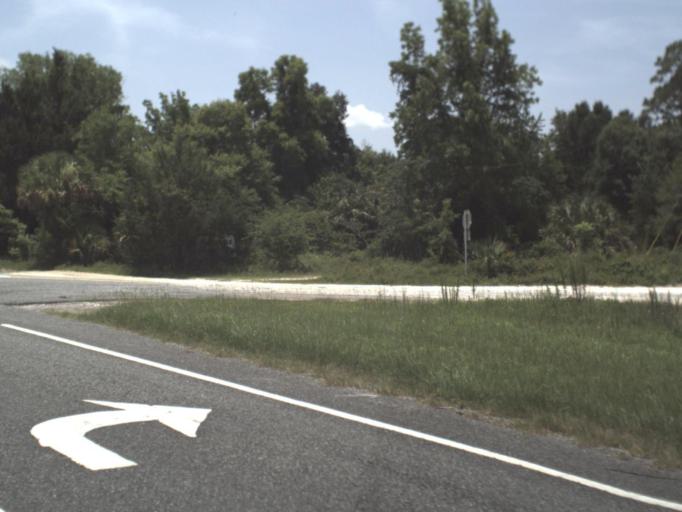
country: US
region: Florida
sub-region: Taylor County
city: Steinhatchee
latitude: 29.7792
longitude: -83.3268
